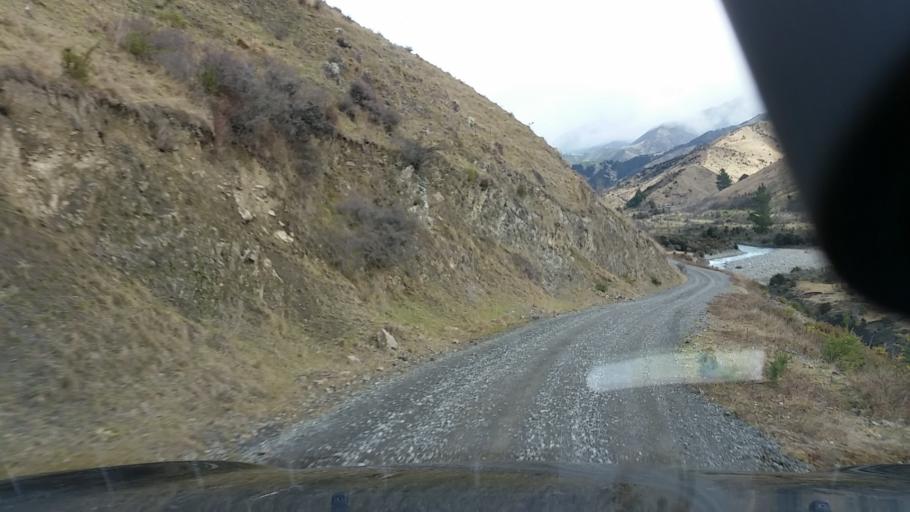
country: NZ
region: Tasman
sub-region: Tasman District
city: Brightwater
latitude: -41.7399
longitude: 173.4178
